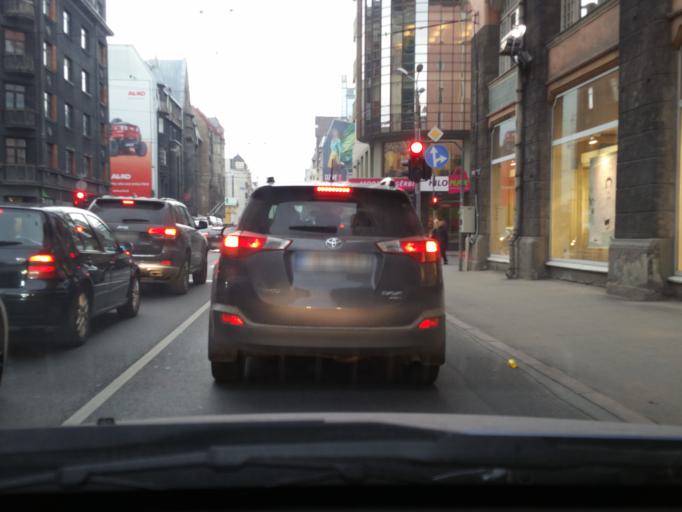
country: LV
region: Riga
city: Riga
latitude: 56.9575
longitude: 24.1233
